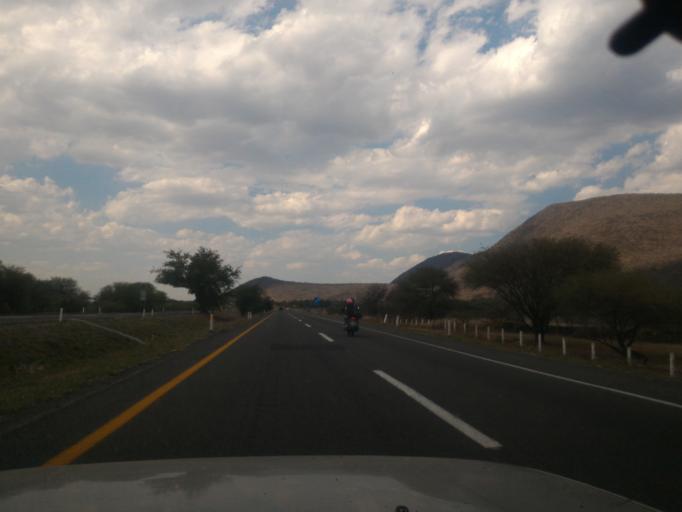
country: MX
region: Jalisco
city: Zacoalco de Torres
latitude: 20.1768
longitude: -103.5095
